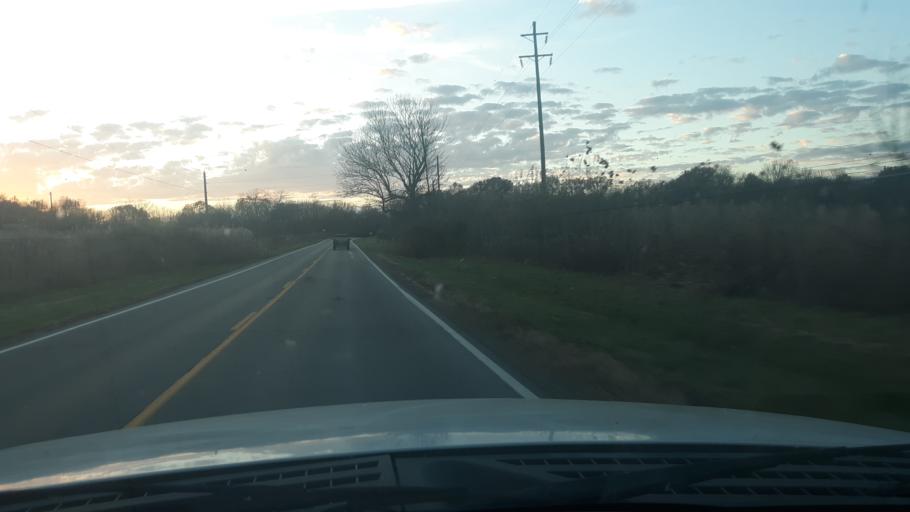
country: US
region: Illinois
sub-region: Saline County
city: Harrisburg
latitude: 37.8347
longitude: -88.5844
